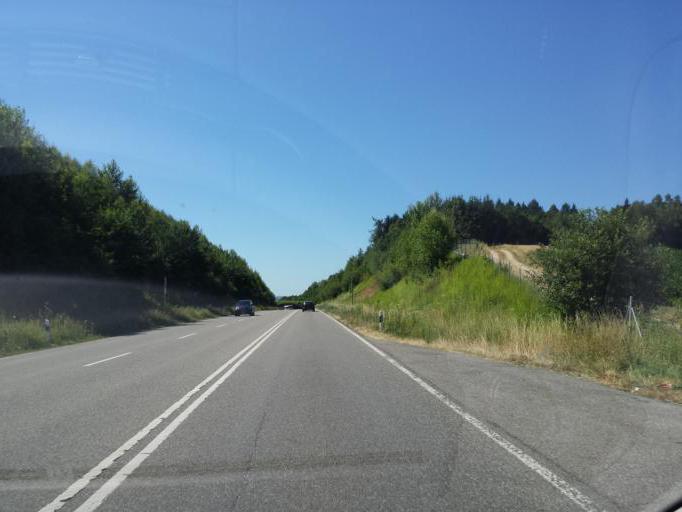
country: DE
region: Baden-Wuerttemberg
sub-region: Freiburg Region
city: Bodman-Ludwigshafen
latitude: 47.8368
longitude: 9.0486
